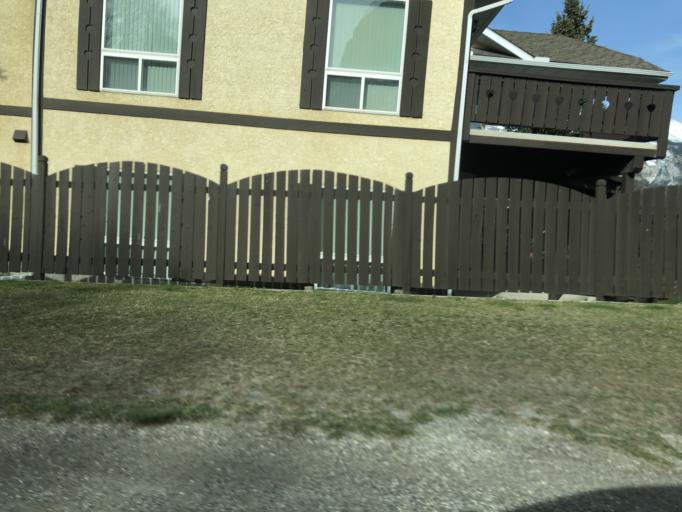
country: CA
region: Alberta
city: Canmore
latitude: 51.0810
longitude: -115.3671
